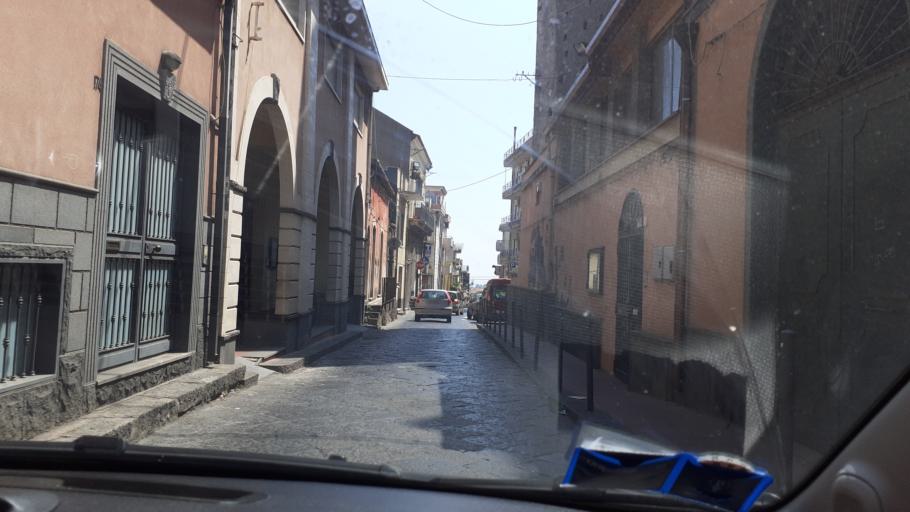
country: IT
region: Sicily
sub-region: Catania
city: Misterbianco
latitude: 37.5192
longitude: 15.0099
